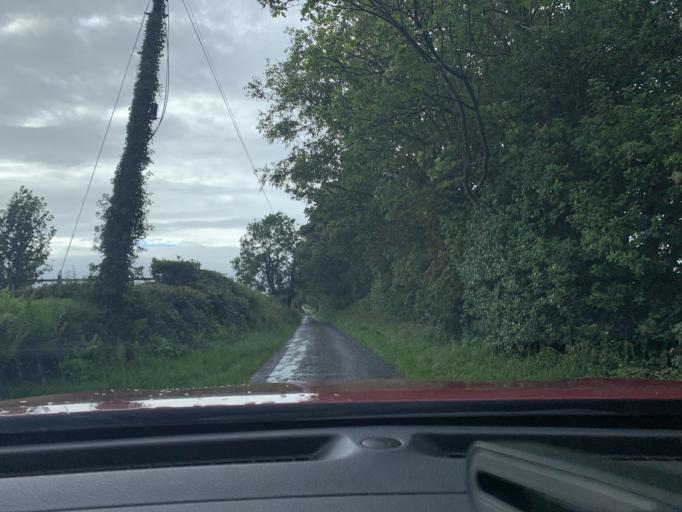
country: IE
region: Connaught
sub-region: Sligo
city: Strandhill
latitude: 54.3575
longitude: -8.5503
